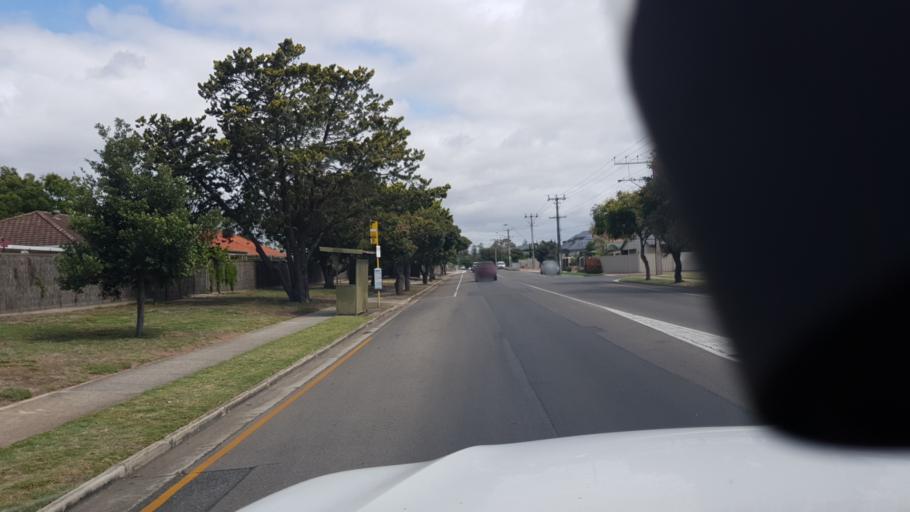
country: AU
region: South Australia
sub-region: Holdfast Bay
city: Glenelg East
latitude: -34.9697
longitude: 138.5284
